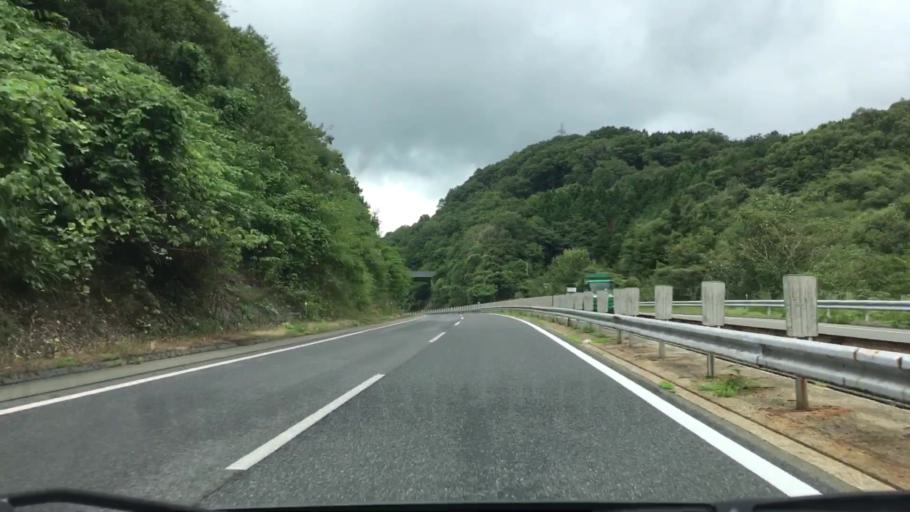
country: JP
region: Okayama
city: Niimi
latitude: 34.8886
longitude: 133.2648
